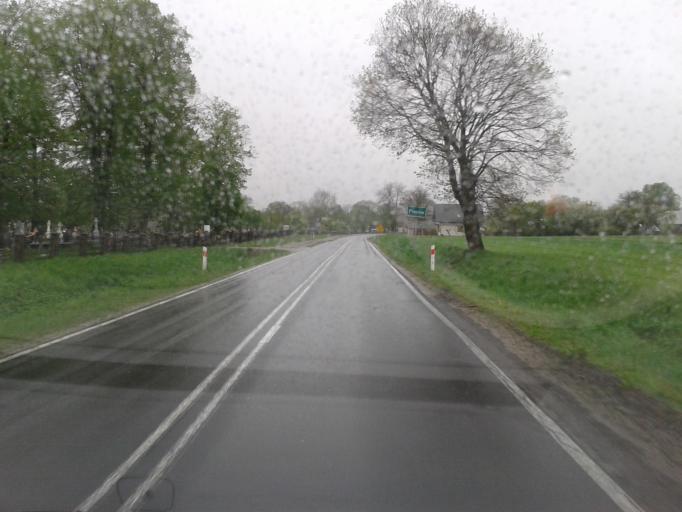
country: PL
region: Subcarpathian Voivodeship
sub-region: Powiat lubaczowski
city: Narol
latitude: 50.3162
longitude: 23.2477
